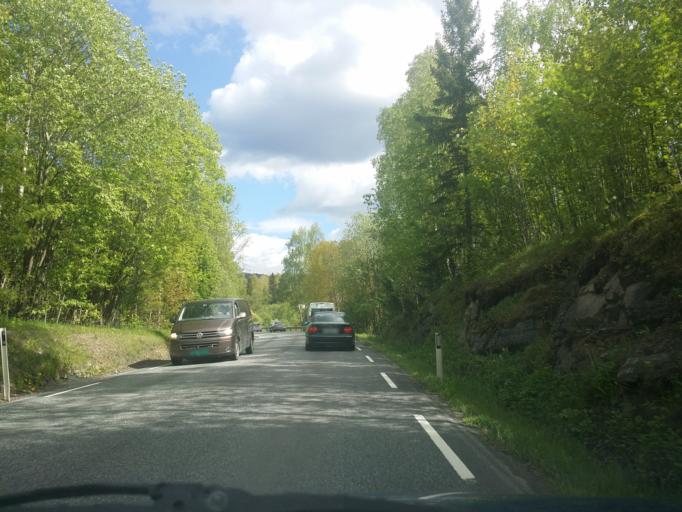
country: NO
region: Oppland
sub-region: Jevnaker
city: Jevnaker
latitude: 60.2665
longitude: 10.4846
